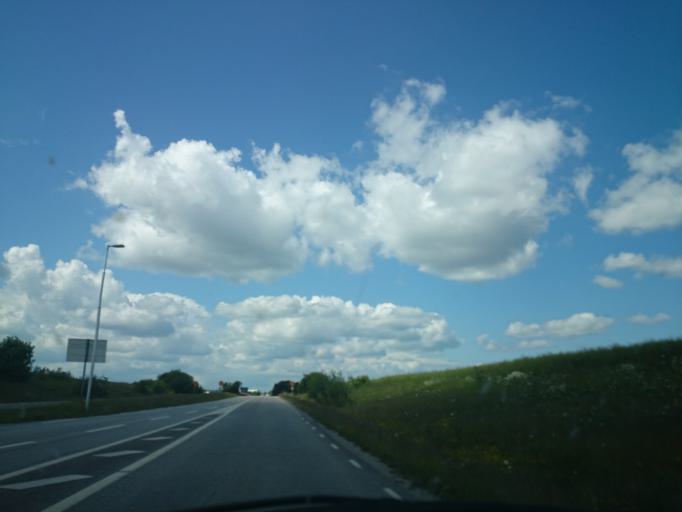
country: SE
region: Skane
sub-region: Lunds Kommun
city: Lund
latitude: 55.7057
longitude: 13.2532
